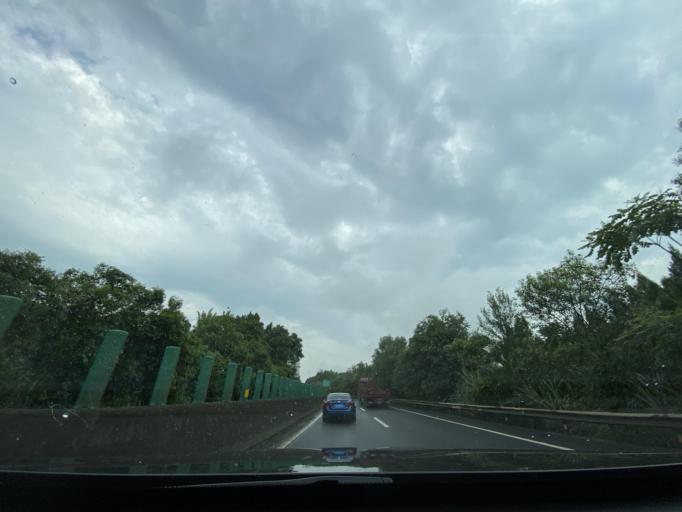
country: CN
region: Sichuan
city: Yanjiang
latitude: 30.1179
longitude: 104.5982
